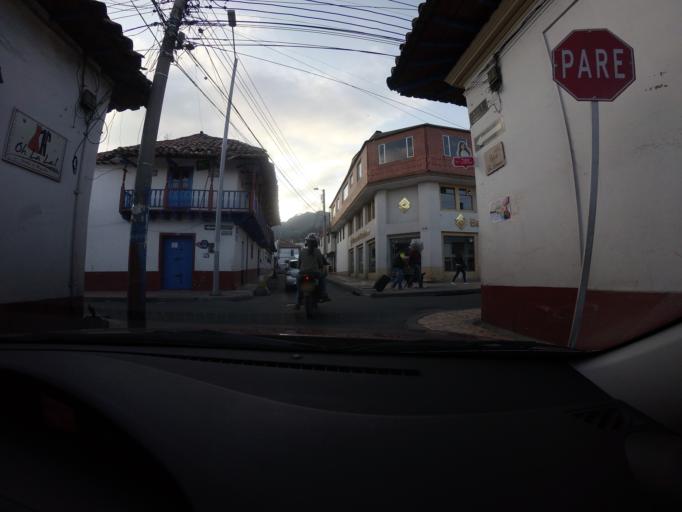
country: CO
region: Cundinamarca
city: Zipaquira
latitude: 5.0228
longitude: -74.0048
